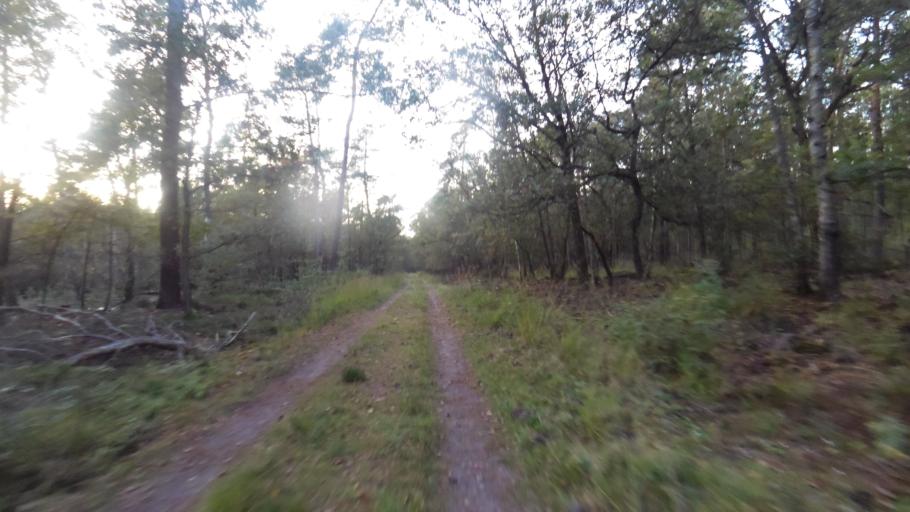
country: NL
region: Gelderland
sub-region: Gemeente Nunspeet
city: Nunspeet
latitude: 52.3282
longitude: 5.7952
